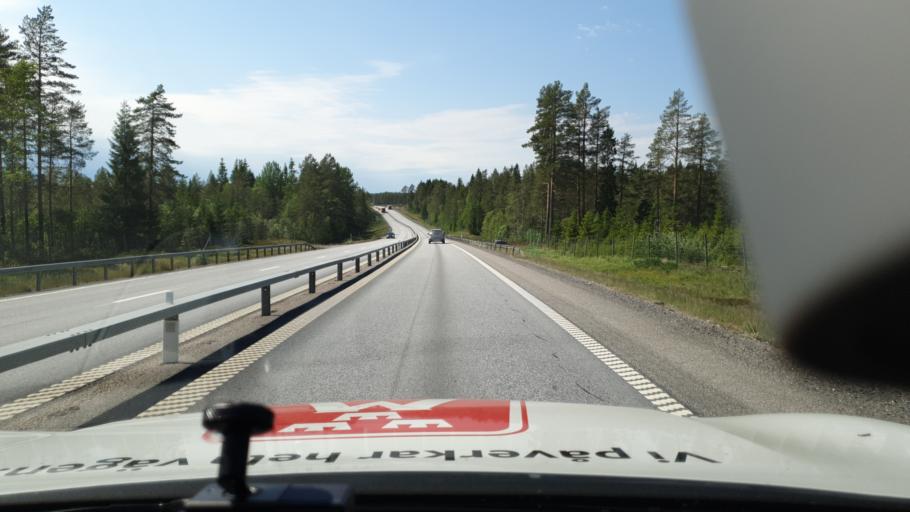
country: SE
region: Vaesterbotten
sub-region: Umea Kommun
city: Hoernefors
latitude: 63.5968
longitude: 19.7197
